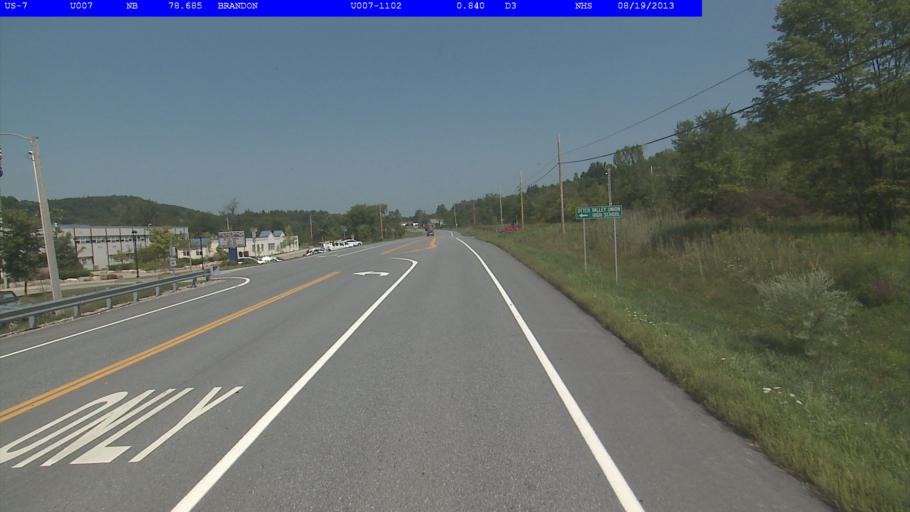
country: US
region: Vermont
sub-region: Rutland County
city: Brandon
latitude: 43.7664
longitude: -73.0503
